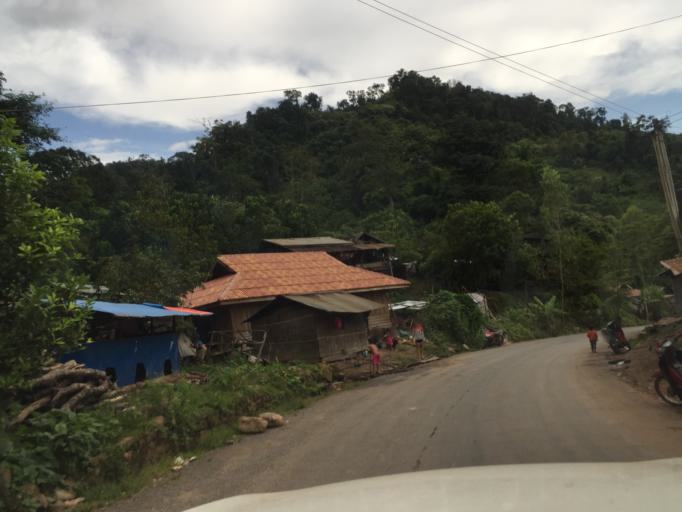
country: LA
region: Phongsali
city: Phongsali
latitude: 21.3459
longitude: 102.0522
